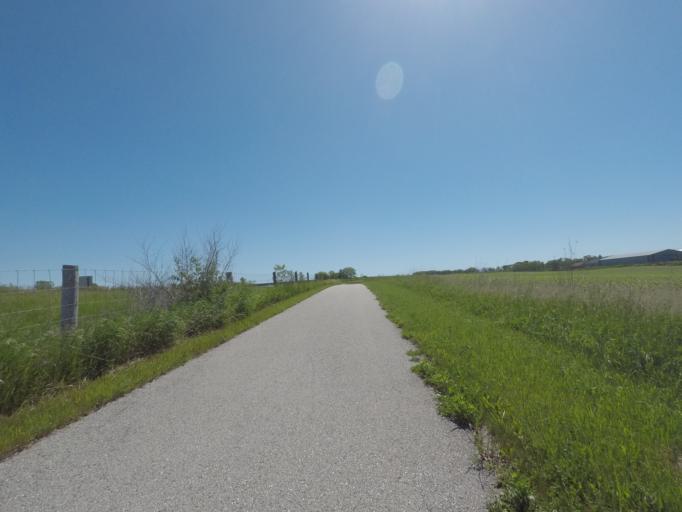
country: US
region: Wisconsin
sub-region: Sheboygan County
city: Kohler
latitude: 43.7501
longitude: -87.8043
